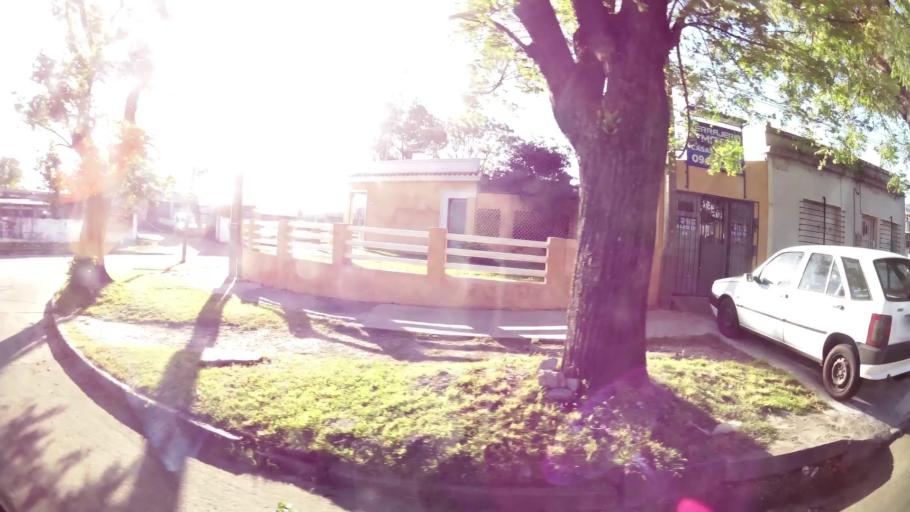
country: UY
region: Montevideo
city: Montevideo
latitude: -34.8786
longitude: -56.1273
